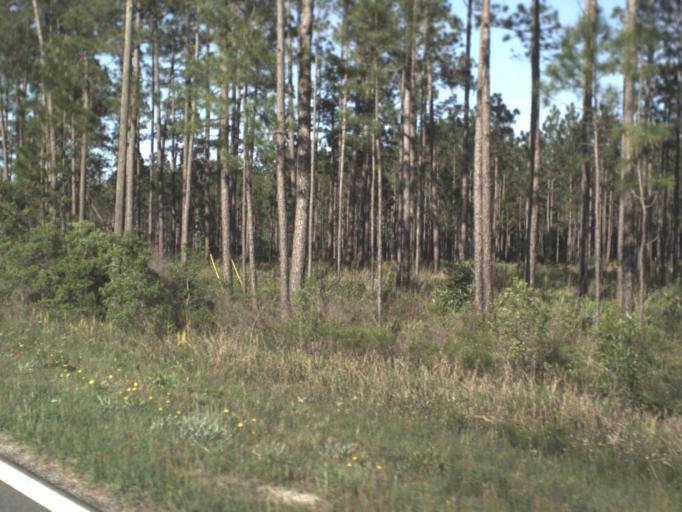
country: US
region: Florida
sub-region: Liberty County
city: Bristol
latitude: 30.2925
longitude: -84.8348
